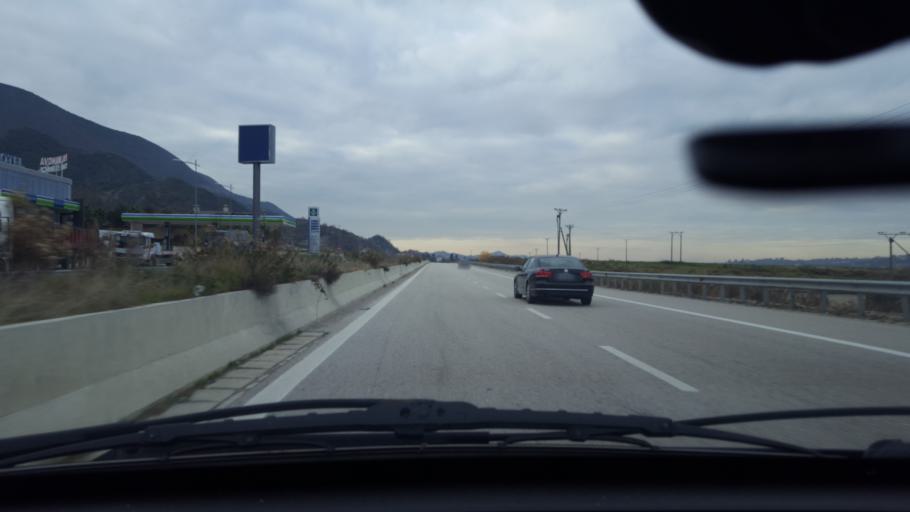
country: AL
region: Tirane
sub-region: Rrethi i Tiranes
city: Berzhite
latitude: 41.2481
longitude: 19.9051
